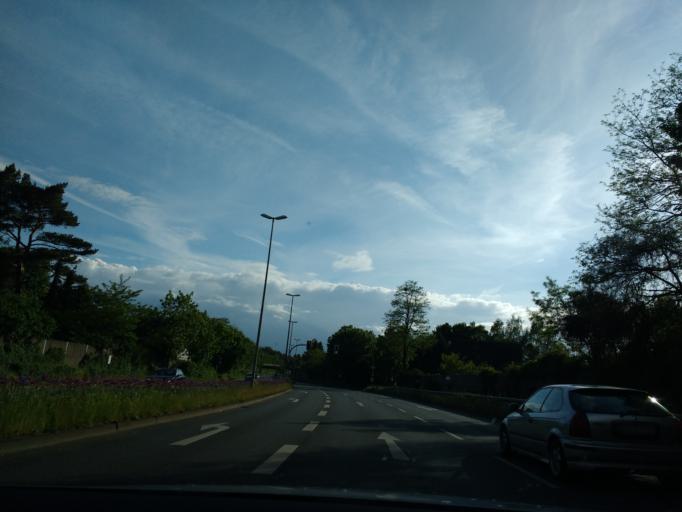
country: DE
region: North Rhine-Westphalia
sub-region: Regierungsbezirk Detmold
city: Bad Salzuflen
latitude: 52.0720
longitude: 8.7470
